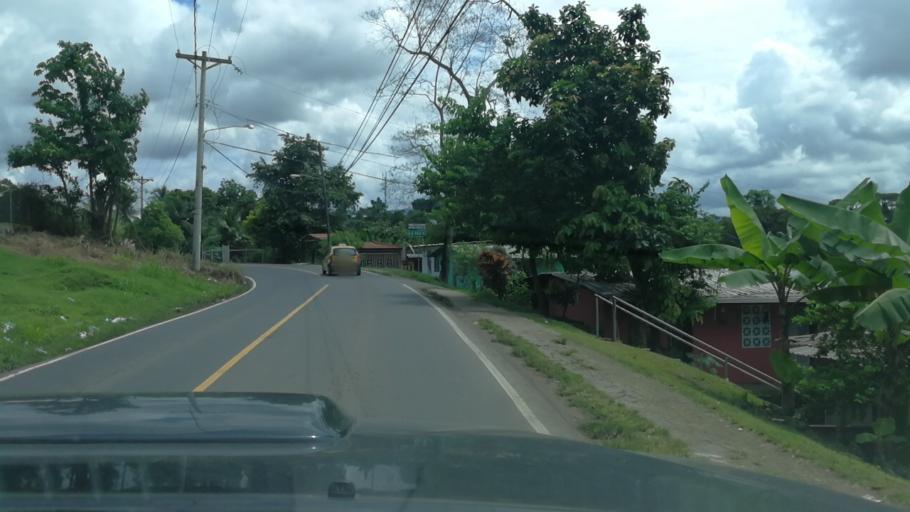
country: PA
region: Panama
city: Tocumen
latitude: 9.0766
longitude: -79.4289
